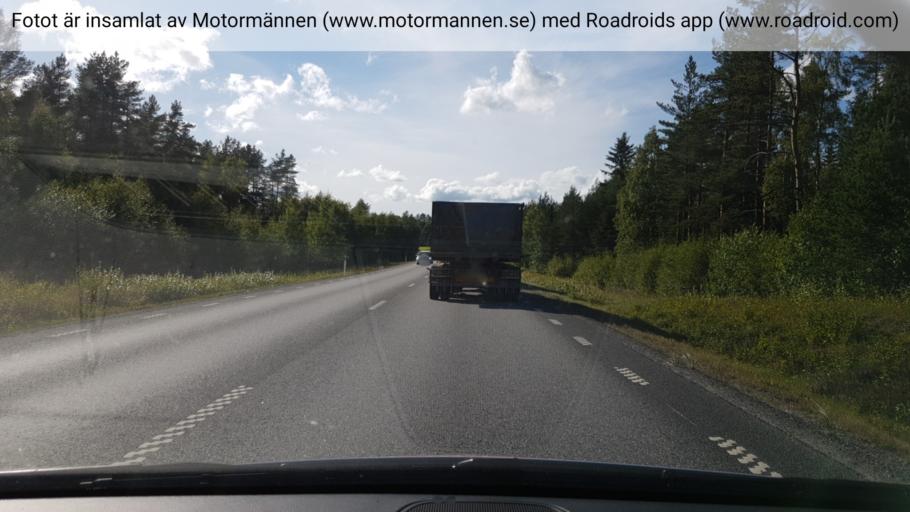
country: SE
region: Vaesterbotten
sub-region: Umea Kommun
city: Roback
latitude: 63.8469
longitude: 20.1477
